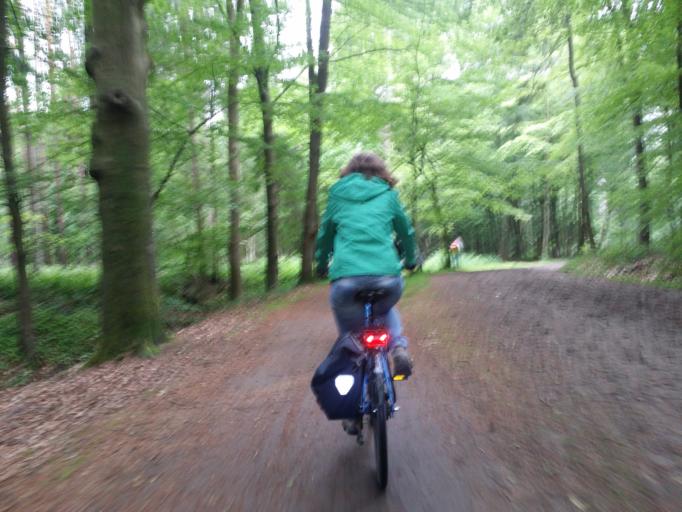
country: DE
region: Lower Saxony
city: Rastede
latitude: 53.2359
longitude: 8.2309
